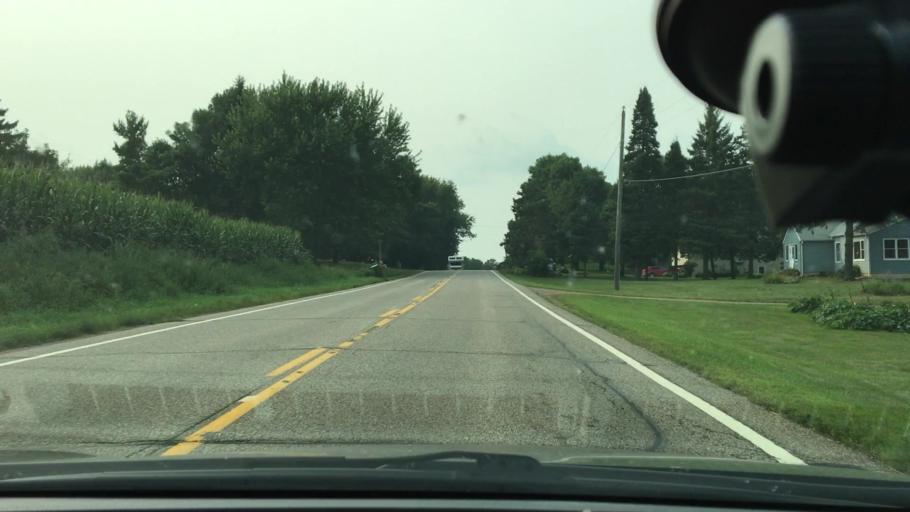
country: US
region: Minnesota
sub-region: Hennepin County
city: Dayton
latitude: 45.2259
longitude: -93.4898
